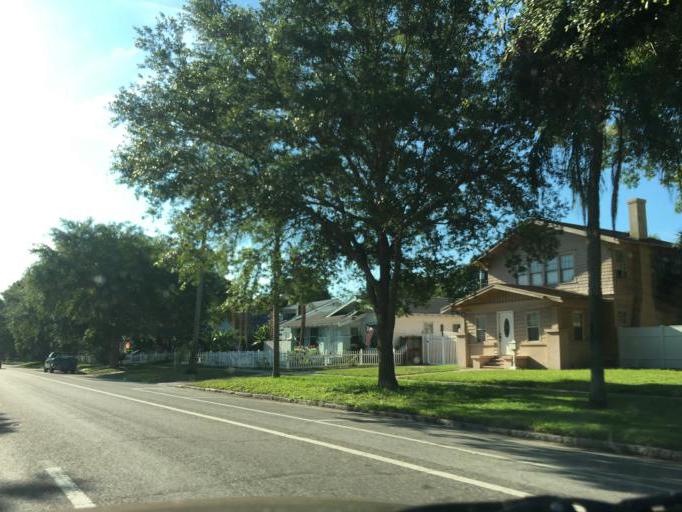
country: US
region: Florida
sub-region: Pinellas County
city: Saint Petersburg
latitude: 27.7702
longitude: -82.6685
